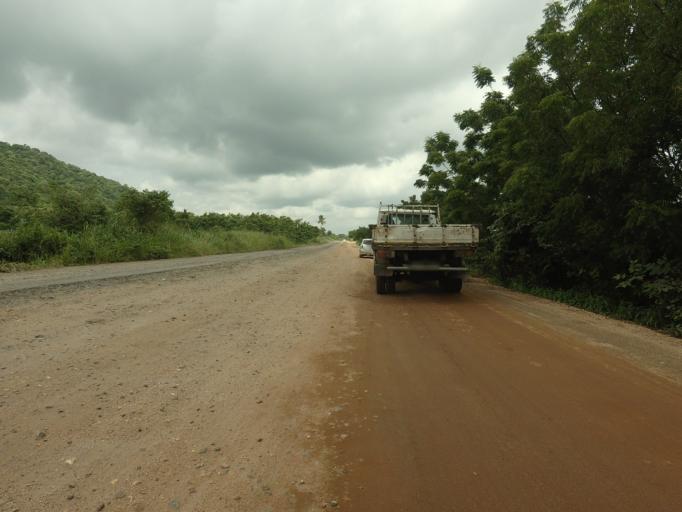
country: GH
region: Volta
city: Ho
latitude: 6.6519
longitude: 0.3012
